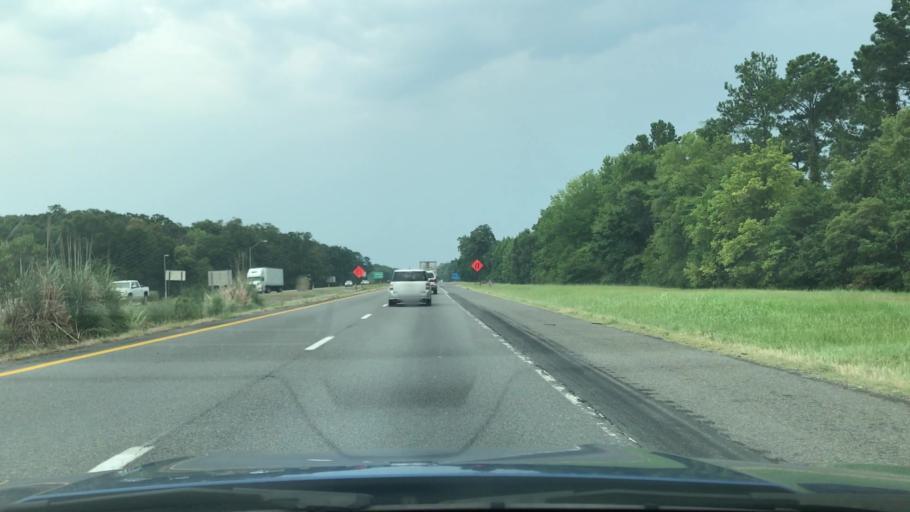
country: US
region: Texas
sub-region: Harrison County
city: Waskom
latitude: 32.4623
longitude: -94.0454
